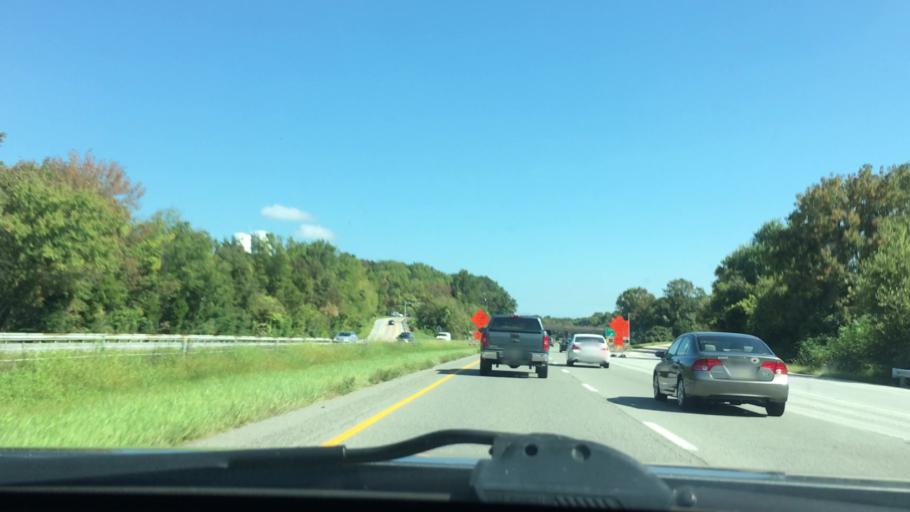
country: US
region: Pennsylvania
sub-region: Chester County
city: Exton
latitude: 40.0026
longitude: -75.5842
